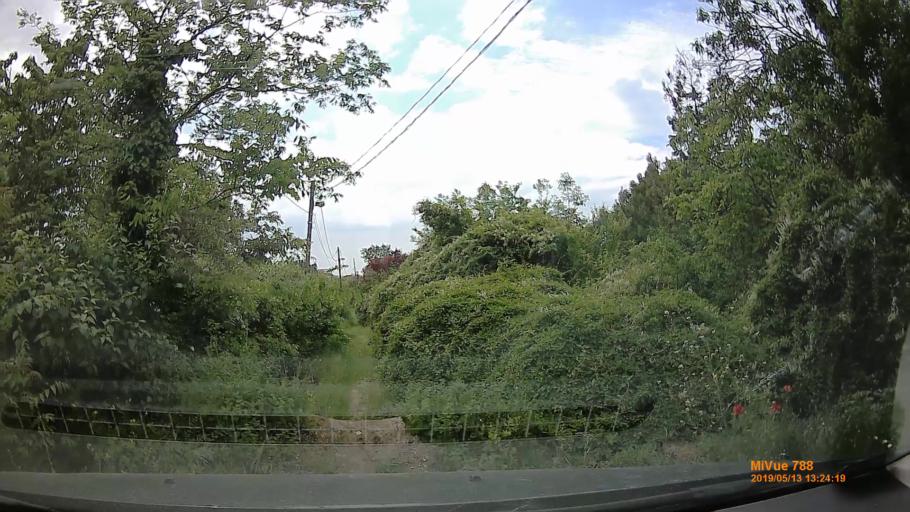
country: HU
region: Budapest
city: Budapest XXII. keruelet
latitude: 47.4144
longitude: 19.0022
